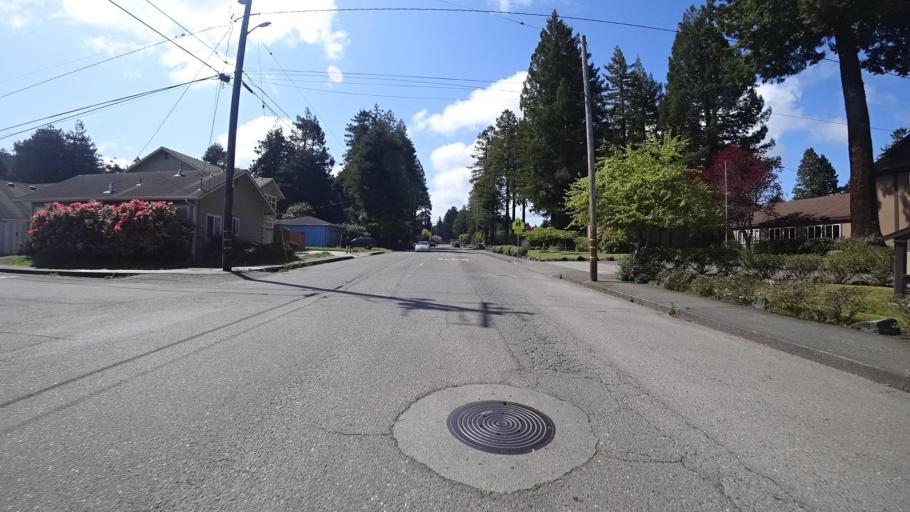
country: US
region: California
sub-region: Humboldt County
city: Cutten
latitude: 40.7794
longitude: -124.1397
